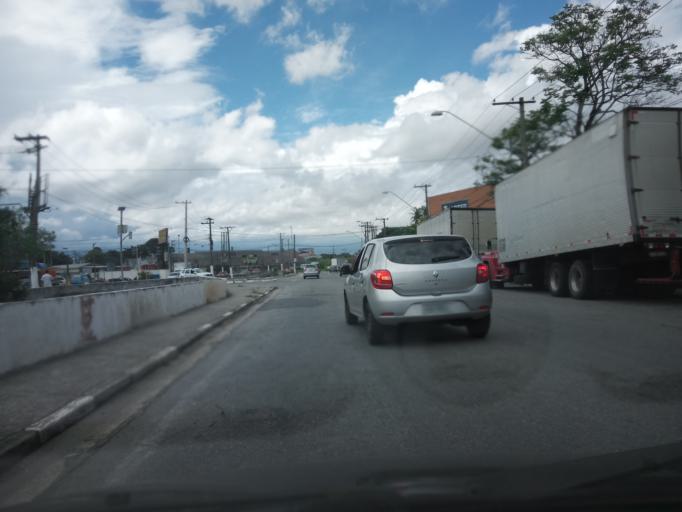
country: BR
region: Sao Paulo
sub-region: Sao Bernardo Do Campo
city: Sao Bernardo do Campo
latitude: -23.6919
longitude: -46.5794
